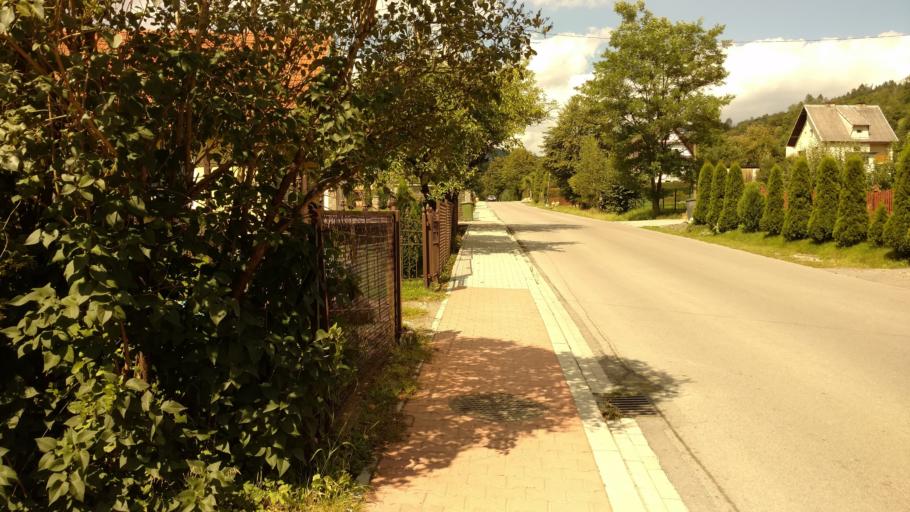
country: PL
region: Lesser Poland Voivodeship
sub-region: Powiat myslenicki
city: Skomielna Czarna
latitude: 49.7303
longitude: 19.8293
